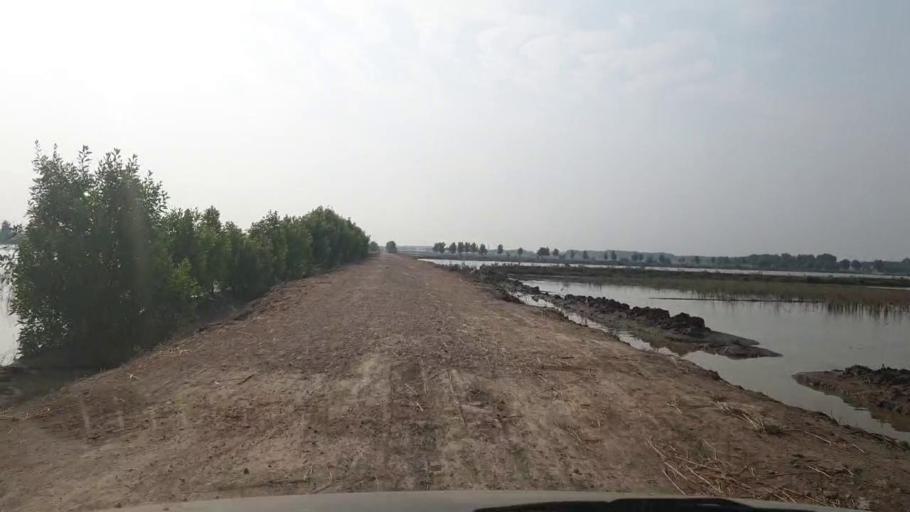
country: PK
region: Sindh
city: Tando Muhammad Khan
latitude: 25.0992
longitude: 68.5071
